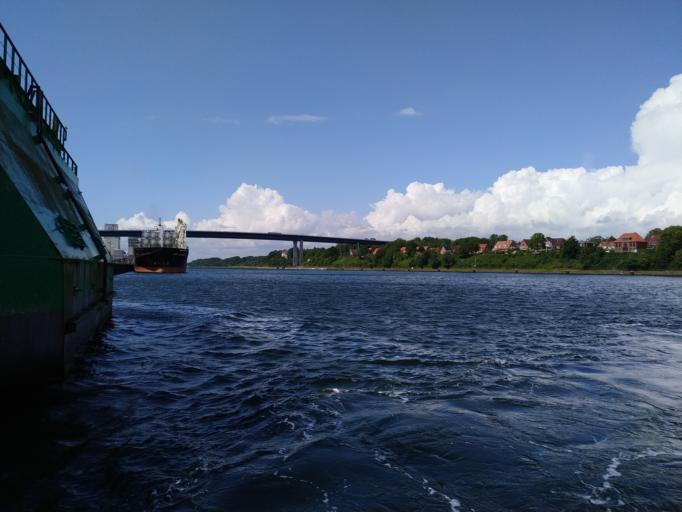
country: DE
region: Schleswig-Holstein
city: Altenholz
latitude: 54.3665
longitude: 10.1316
